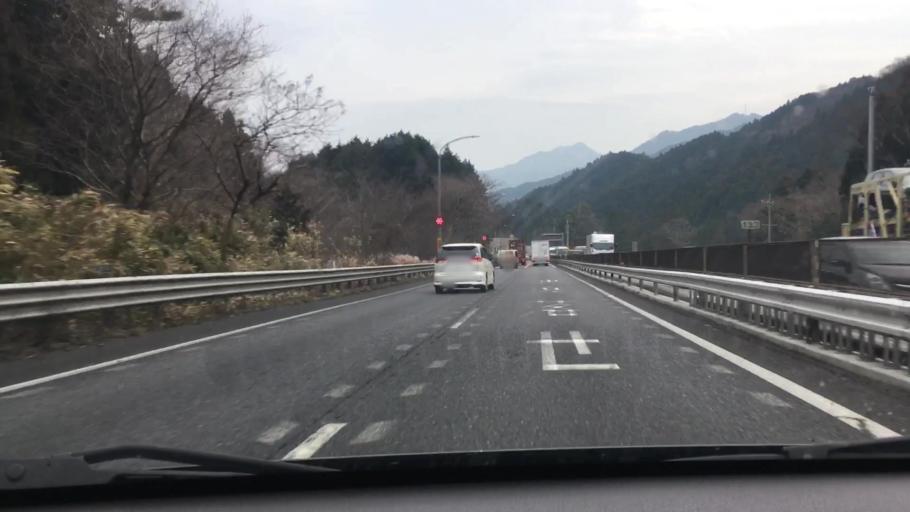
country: JP
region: Mie
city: Kameyama
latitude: 34.8349
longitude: 136.2920
